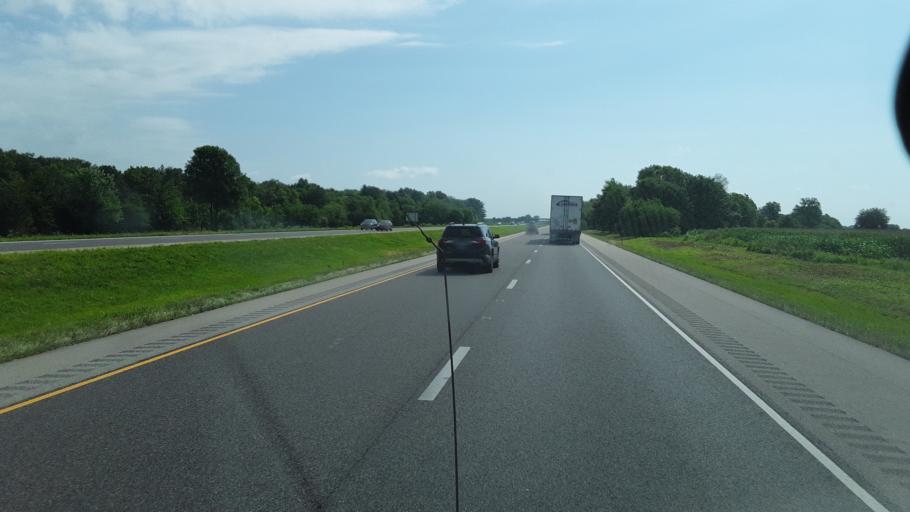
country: US
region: Illinois
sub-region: Fayette County
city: Saint Elmo
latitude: 39.0167
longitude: -88.8382
